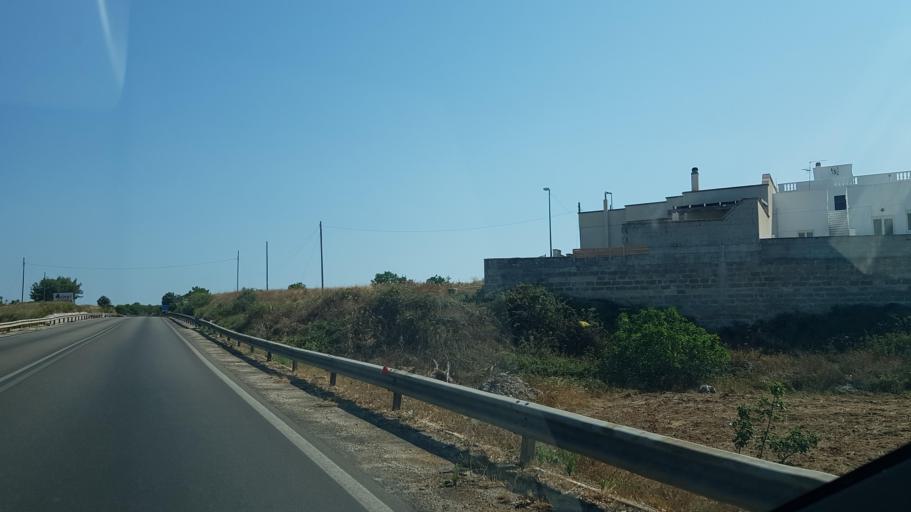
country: IT
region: Apulia
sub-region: Provincia di Lecce
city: Nociglia
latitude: 40.0407
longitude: 18.3213
